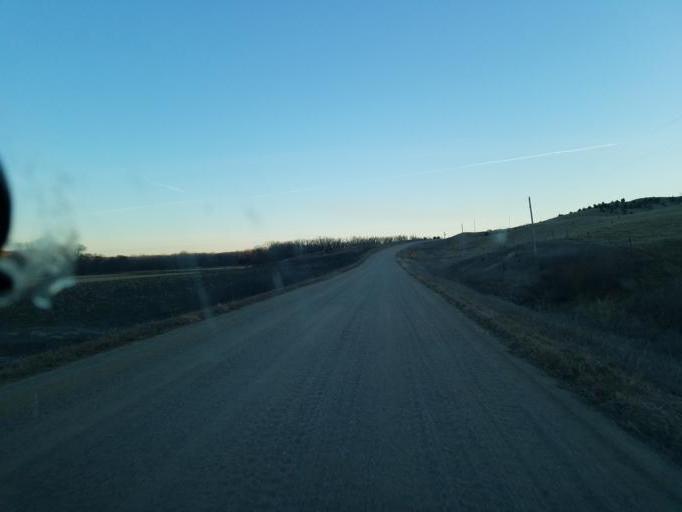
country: US
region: Nebraska
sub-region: Knox County
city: Center
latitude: 42.6862
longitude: -97.8986
